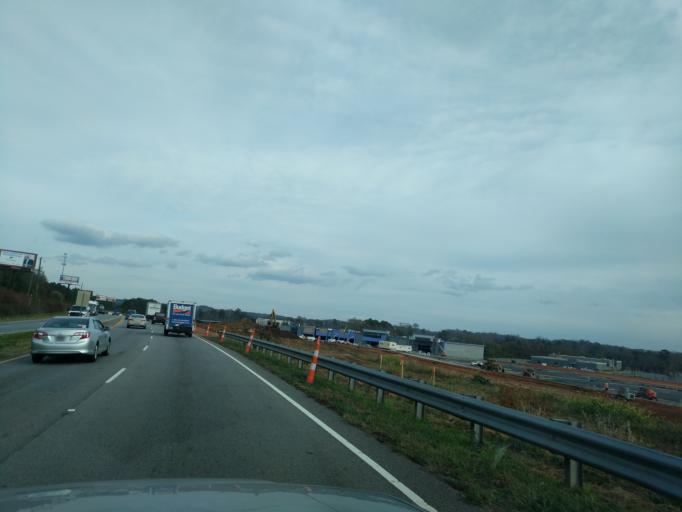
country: US
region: South Carolina
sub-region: Pickens County
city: Clemson
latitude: 34.6903
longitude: -82.8654
